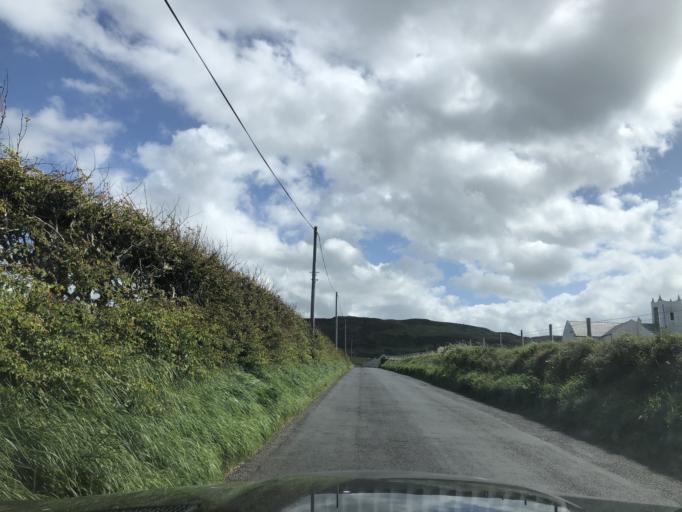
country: GB
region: Northern Ireland
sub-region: Moyle District
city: Ballycastle
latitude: 55.2414
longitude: -6.3664
